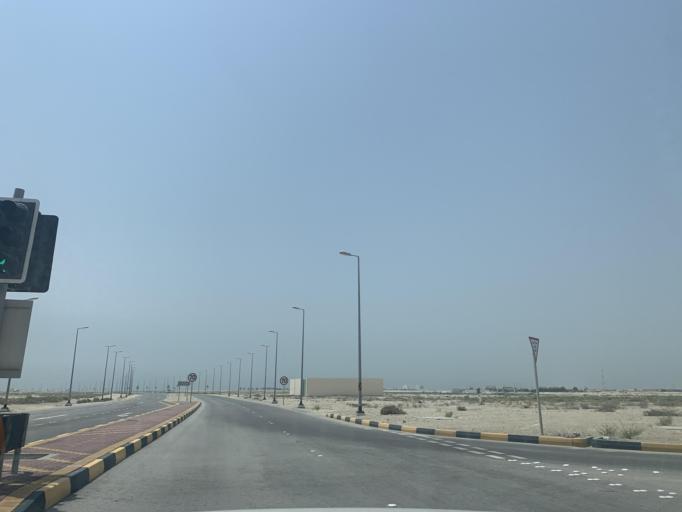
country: BH
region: Central Governorate
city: Dar Kulayb
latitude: 25.8390
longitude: 50.5917
